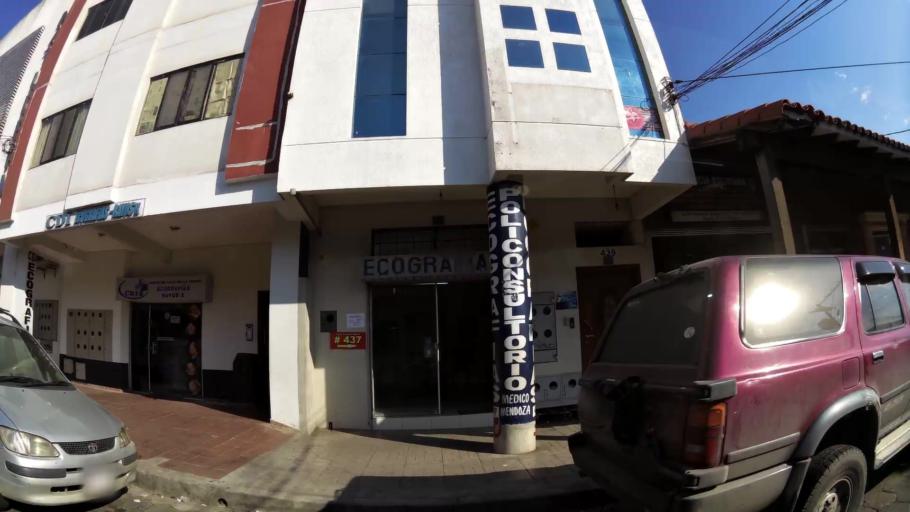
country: BO
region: Santa Cruz
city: Santa Cruz de la Sierra
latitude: -17.7810
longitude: -63.1863
